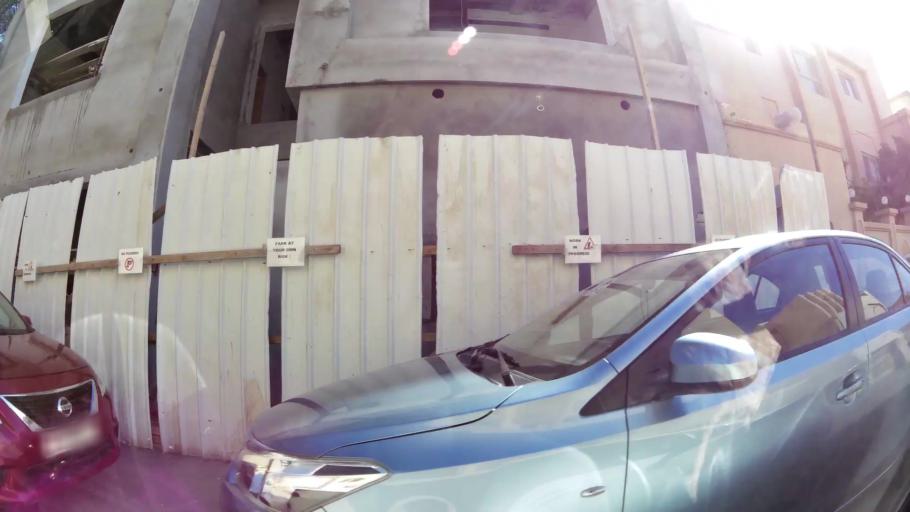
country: BH
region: Muharraq
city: Al Muharraq
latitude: 26.2645
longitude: 50.6200
